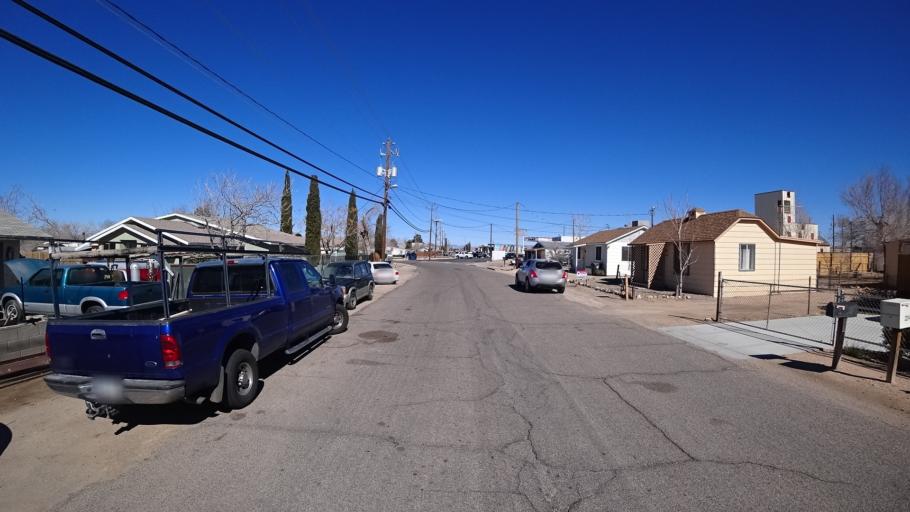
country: US
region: Arizona
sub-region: Mohave County
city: Kingman
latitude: 35.2024
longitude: -114.0258
